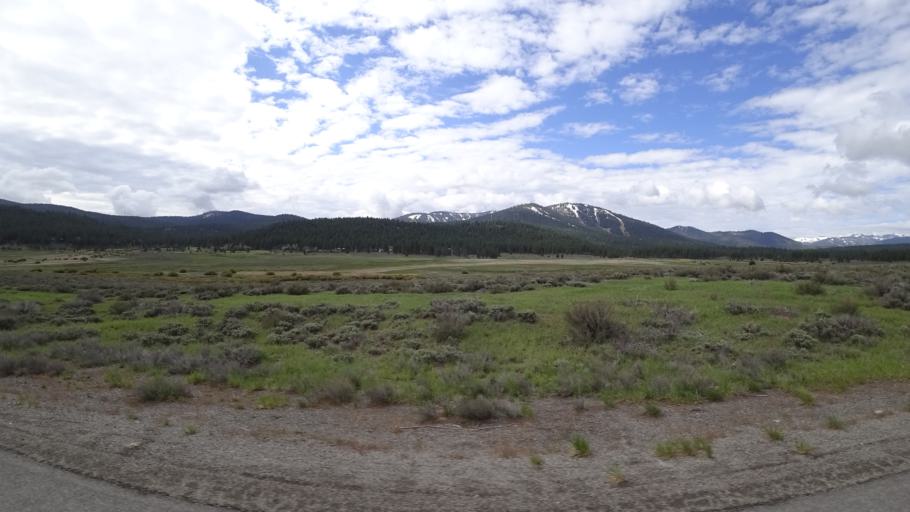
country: US
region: California
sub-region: Nevada County
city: Truckee
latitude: 39.3030
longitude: -120.1271
